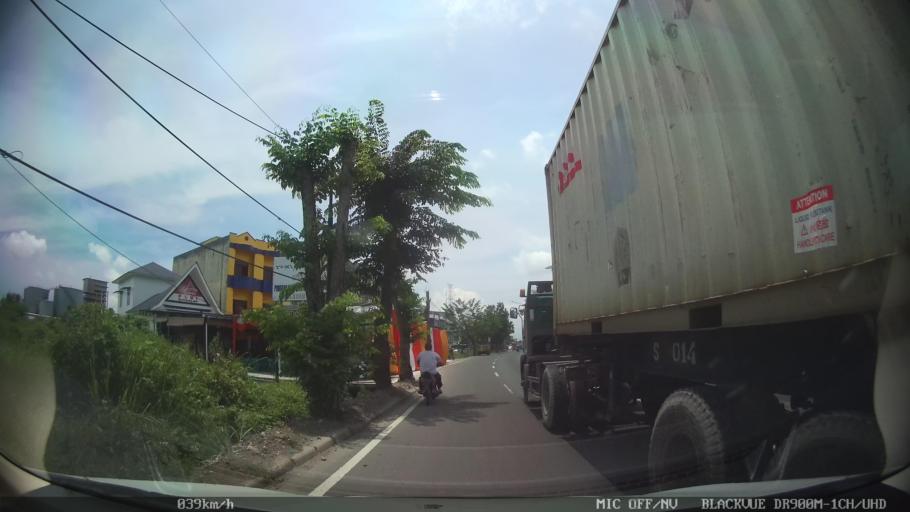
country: ID
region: North Sumatra
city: Labuhan Deli
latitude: 3.7270
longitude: 98.6778
